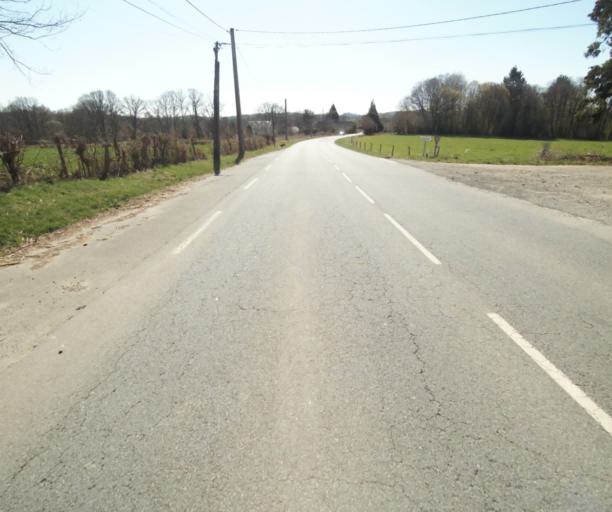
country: FR
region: Limousin
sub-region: Departement de la Correze
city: Saint-Mexant
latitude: 45.3045
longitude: 1.6778
